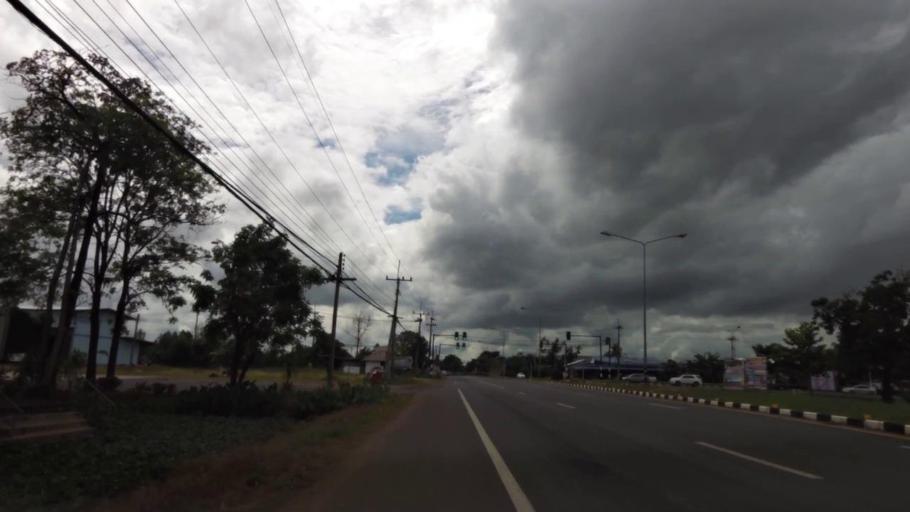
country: TH
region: Nakhon Sawan
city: Phai Sali
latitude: 15.5936
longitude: 100.6567
